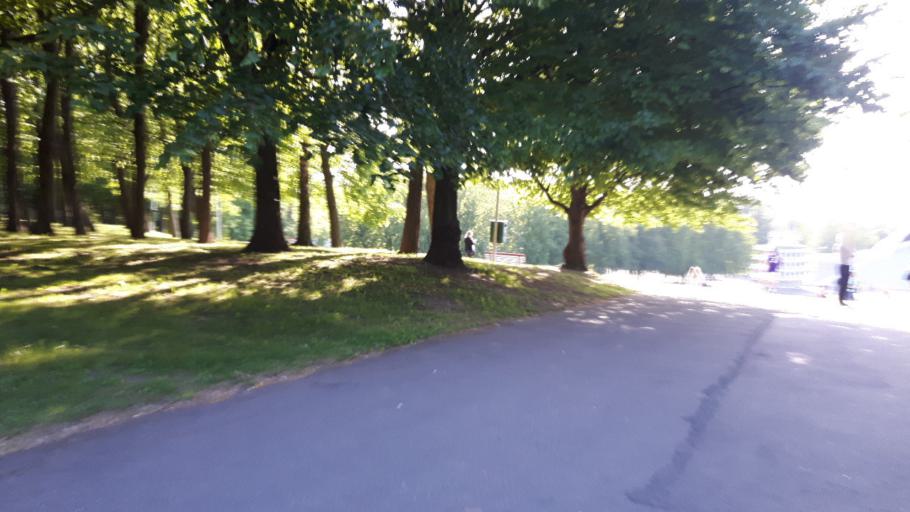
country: EE
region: Harju
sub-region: Tallinna linn
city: Tallinn
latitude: 59.4436
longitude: 24.8105
